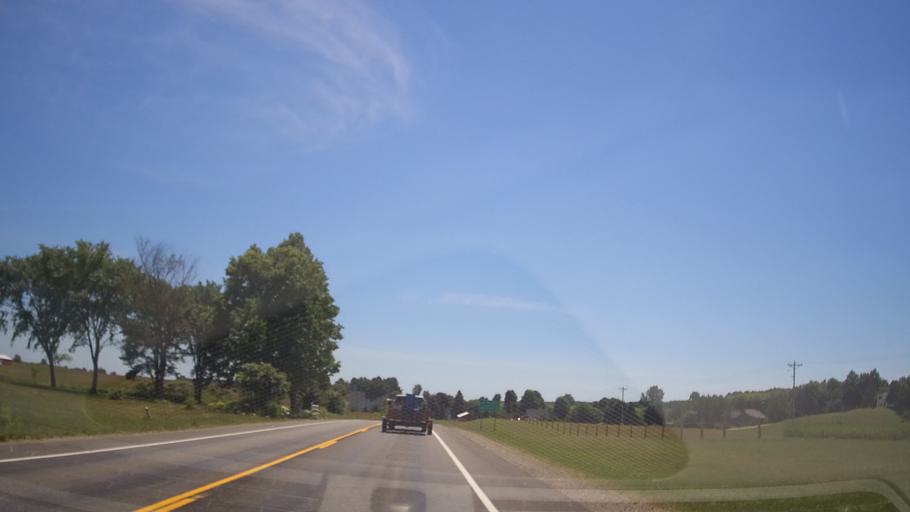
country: US
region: Michigan
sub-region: Grand Traverse County
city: Traverse City
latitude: 44.6177
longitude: -85.6966
